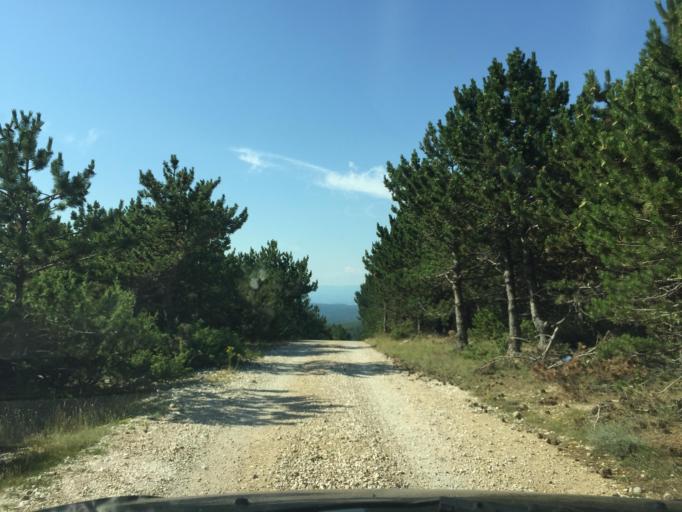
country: HR
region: Primorsko-Goranska
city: Punat
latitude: 45.0185
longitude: 14.6740
